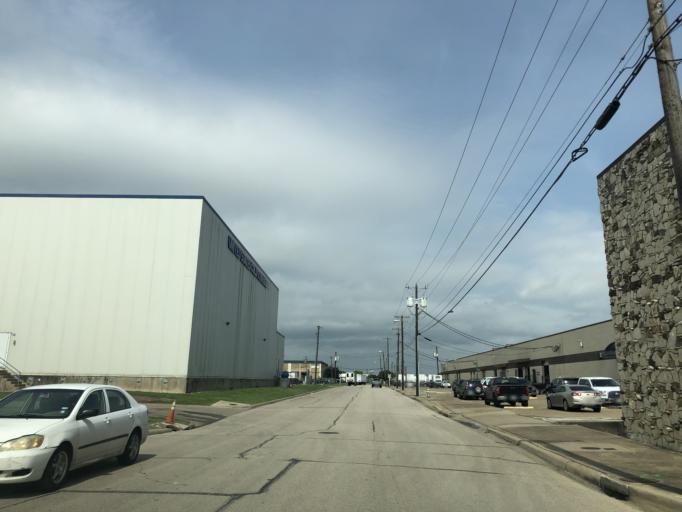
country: US
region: Texas
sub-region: Dallas County
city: Irving
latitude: 32.8121
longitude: -96.8756
